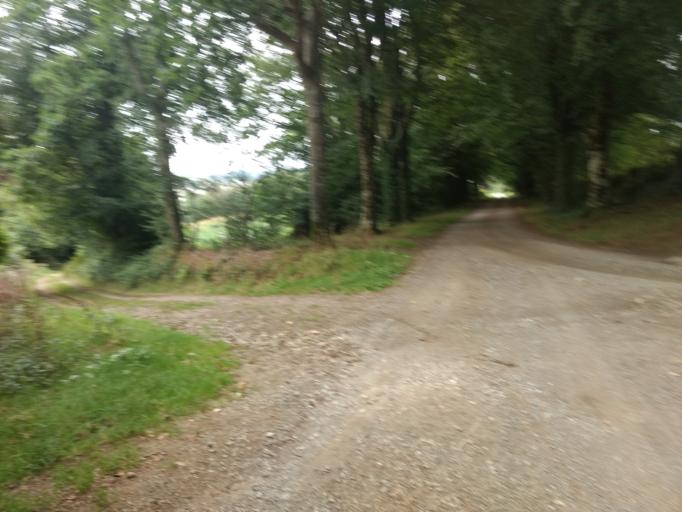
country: FR
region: Brittany
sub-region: Departement du Finistere
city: Loperhet
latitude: 48.3719
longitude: -4.2936
